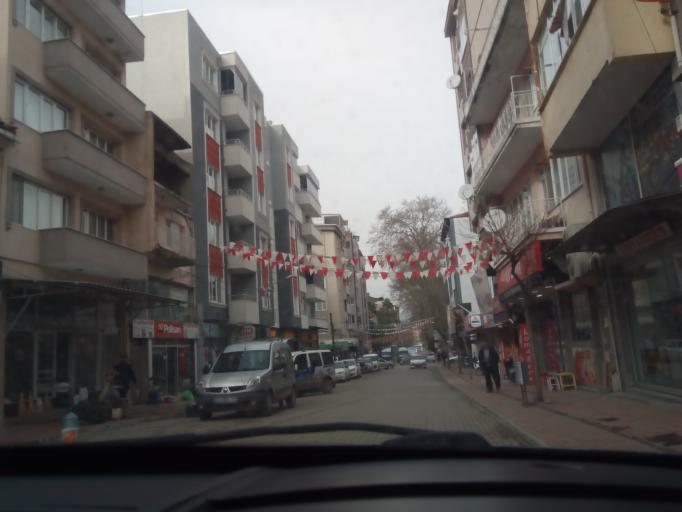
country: TR
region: Balikesir
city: Susurluk
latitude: 39.9160
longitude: 28.1567
